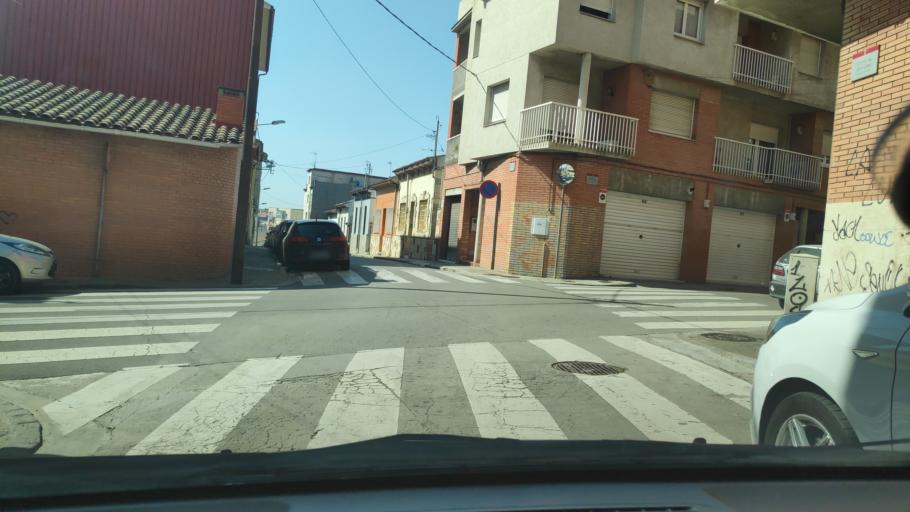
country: ES
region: Catalonia
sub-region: Provincia de Barcelona
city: Mollet del Valles
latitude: 41.5428
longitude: 2.2134
